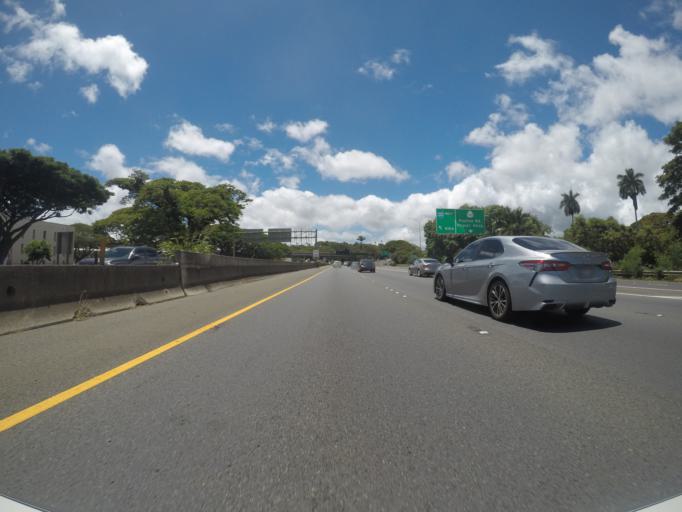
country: US
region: Hawaii
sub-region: Honolulu County
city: Halawa Heights
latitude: 21.3461
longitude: -157.8939
